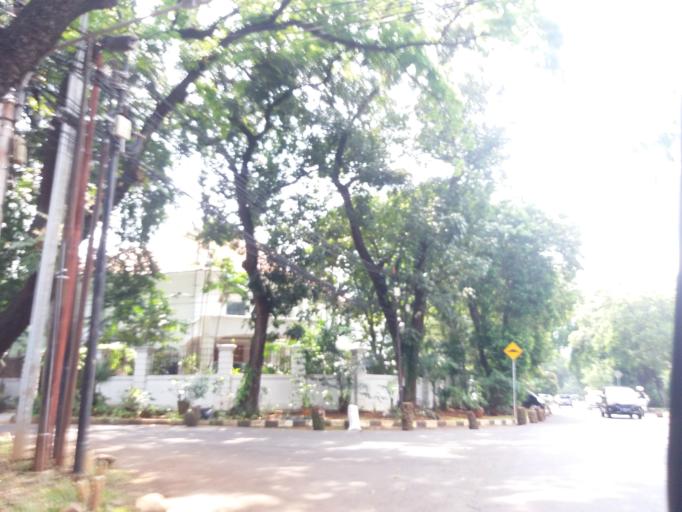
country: ID
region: Jakarta Raya
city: Jakarta
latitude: -6.2320
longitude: 106.8032
